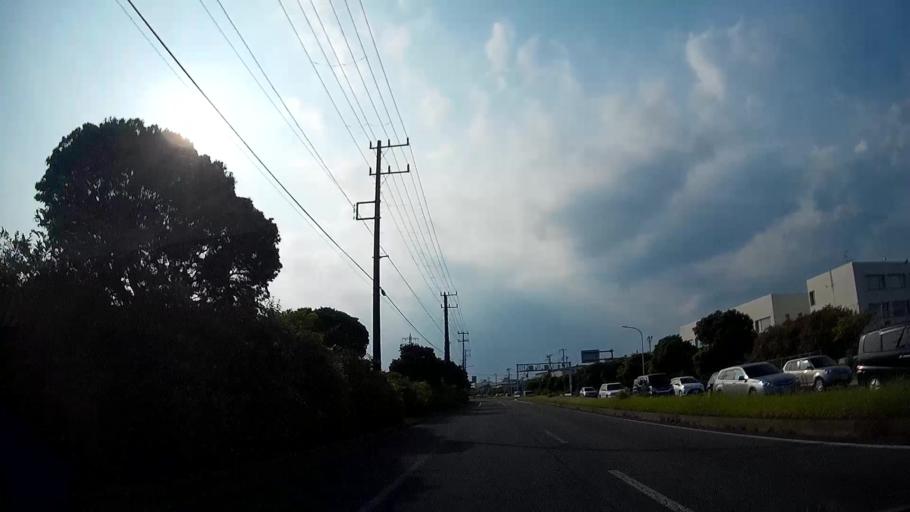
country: JP
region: Chiba
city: Funabashi
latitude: 35.6539
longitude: 140.0236
